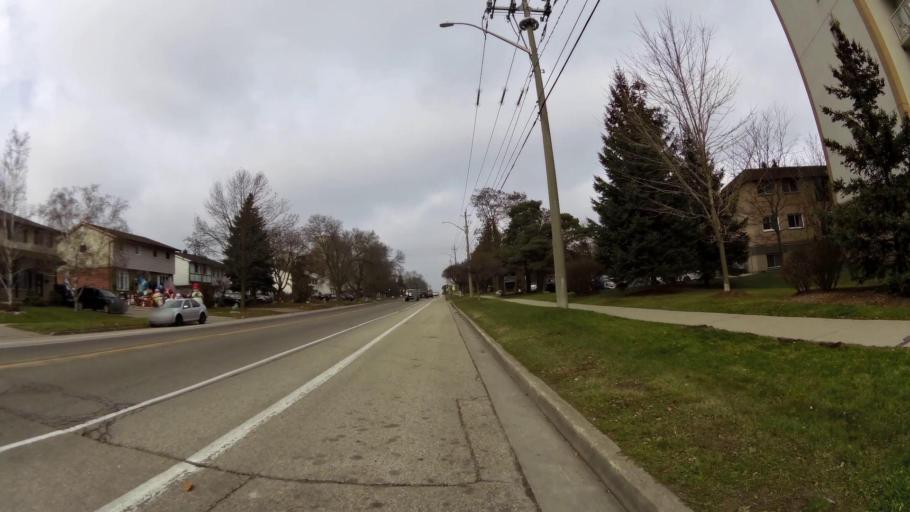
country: CA
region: Ontario
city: Kitchener
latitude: 43.4173
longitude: -80.4814
